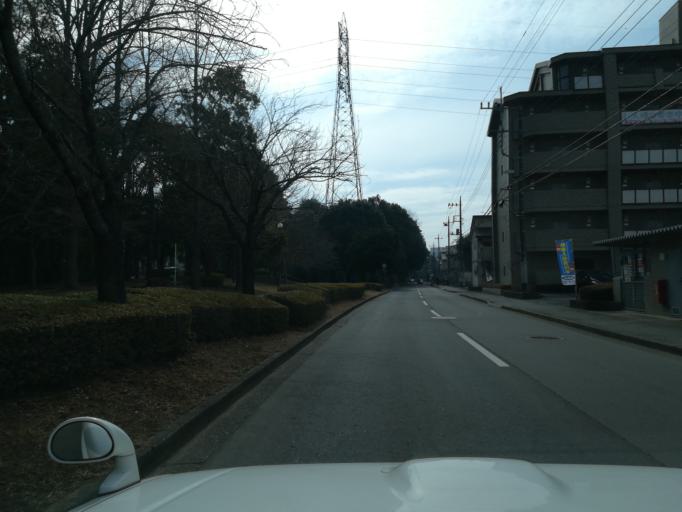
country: JP
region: Ibaraki
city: Naka
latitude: 36.0995
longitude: 140.1014
